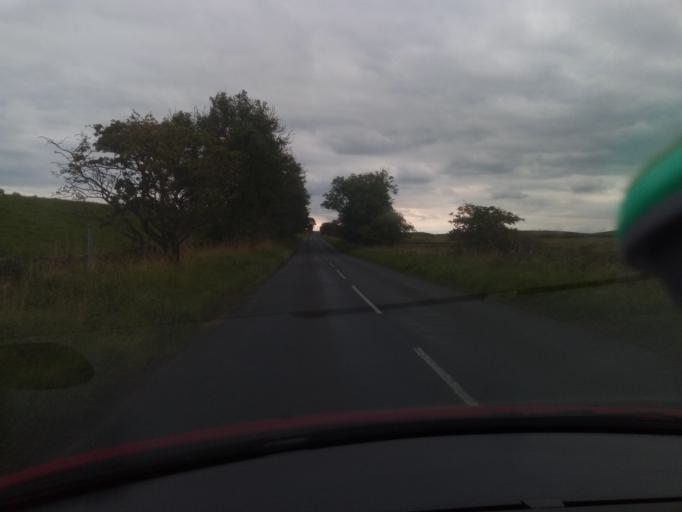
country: GB
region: England
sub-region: Northumberland
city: Warden
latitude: 54.9501
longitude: -2.2001
